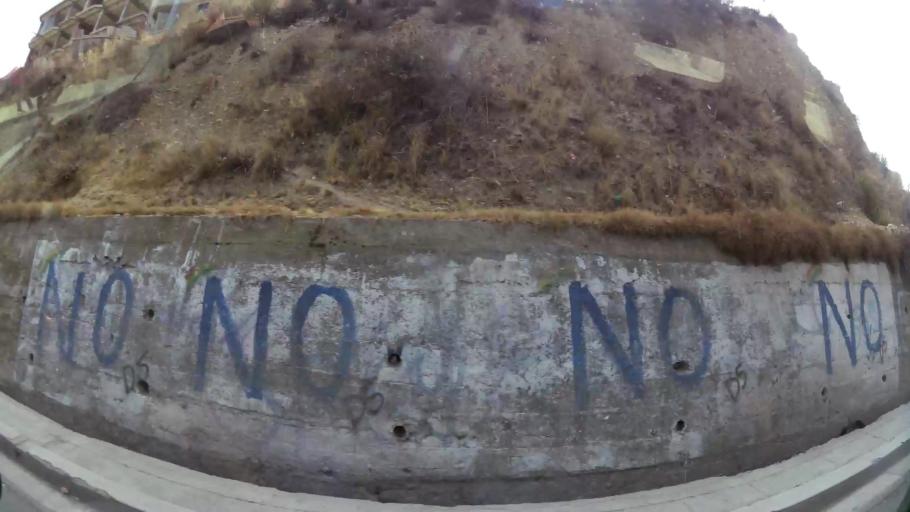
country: BO
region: La Paz
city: La Paz
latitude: -16.4808
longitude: -68.1281
